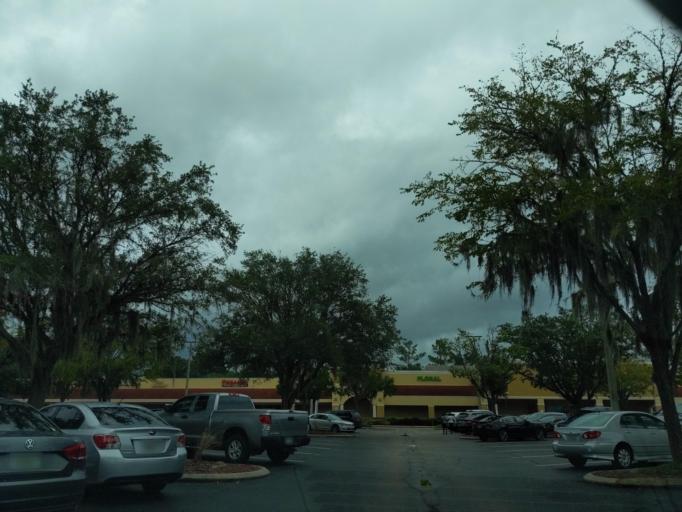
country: US
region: Florida
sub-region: Alachua County
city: Gainesville
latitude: 29.6009
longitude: -82.4208
